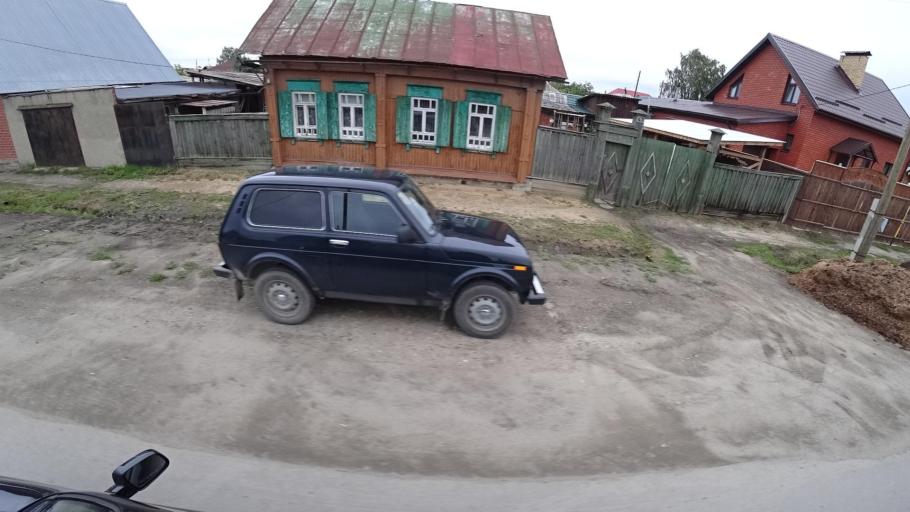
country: RU
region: Sverdlovsk
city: Kamyshlov
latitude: 56.8396
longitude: 62.7292
